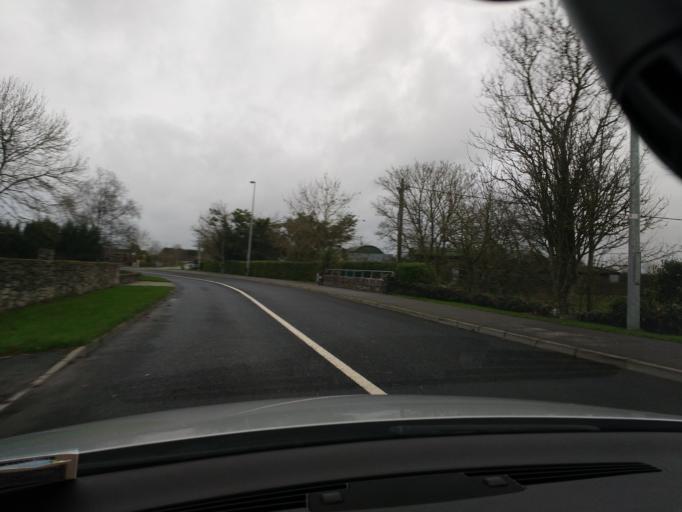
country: IE
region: Munster
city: Thurles
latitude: 52.6725
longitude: -7.7159
